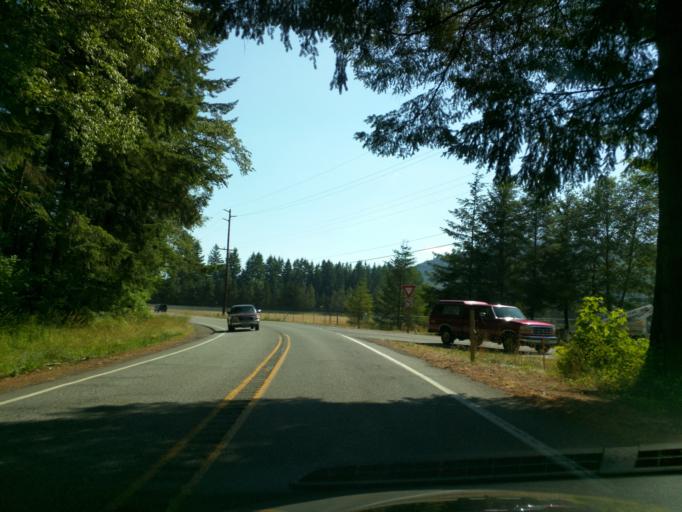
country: US
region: Washington
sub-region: Whatcom County
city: Peaceful Valley
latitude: 48.9165
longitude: -122.1375
